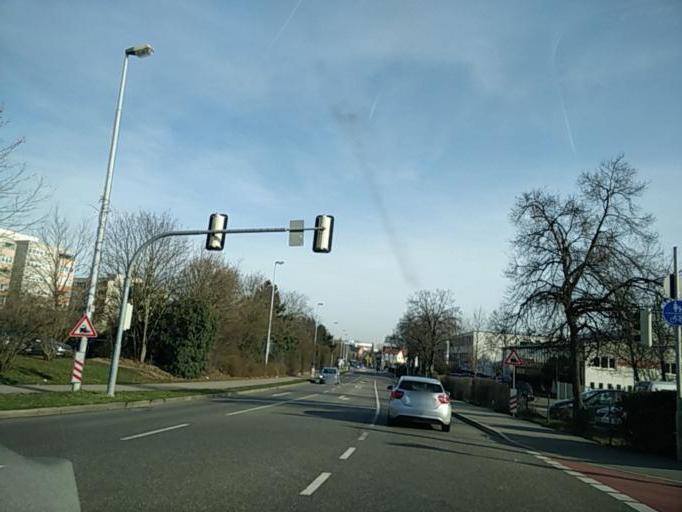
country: DE
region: Baden-Wuerttemberg
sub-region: Regierungsbezirk Stuttgart
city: Boeblingen
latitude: 48.6751
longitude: 9.0116
